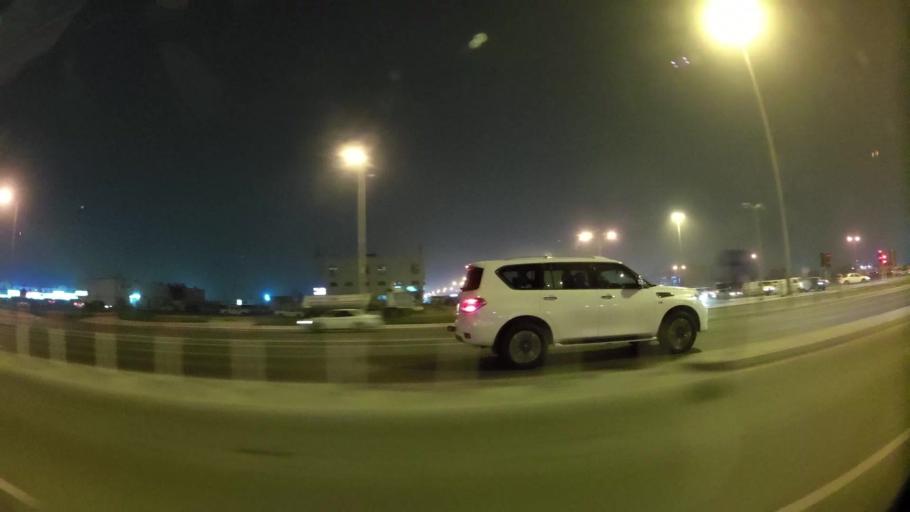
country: QA
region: Baladiyat ad Dawhah
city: Doha
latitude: 25.2487
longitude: 51.4723
